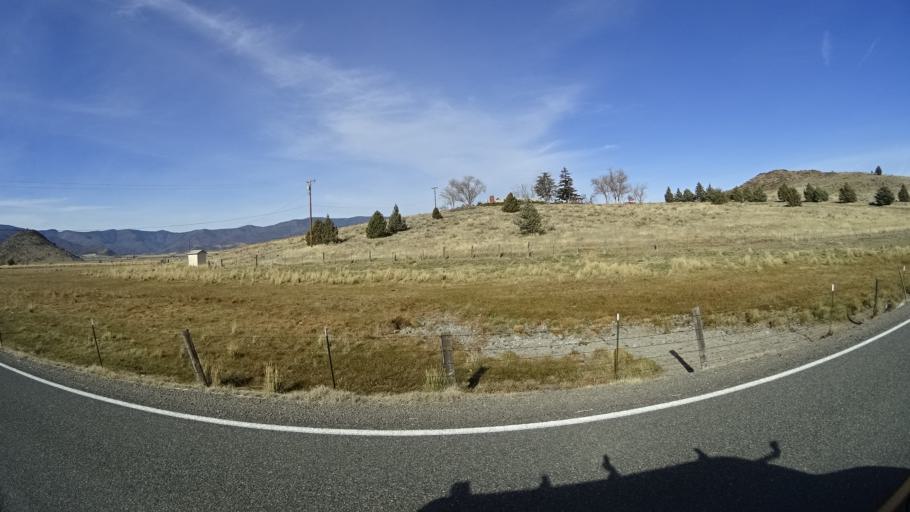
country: US
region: California
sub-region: Siskiyou County
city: Weed
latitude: 41.5362
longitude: -122.5083
